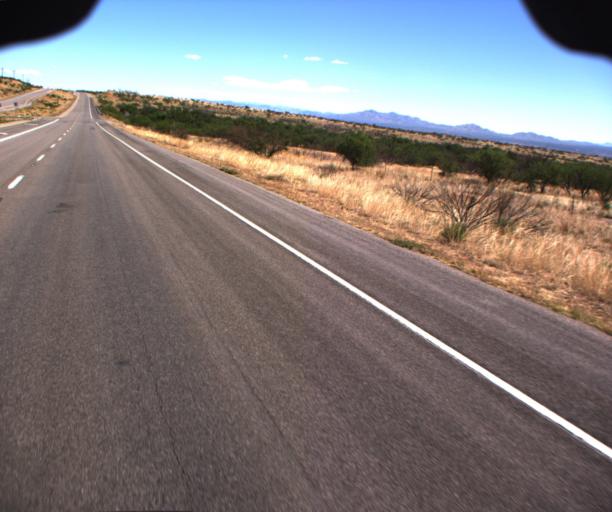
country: US
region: Arizona
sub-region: Cochise County
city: Whetstone
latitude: 31.8378
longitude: -110.3429
